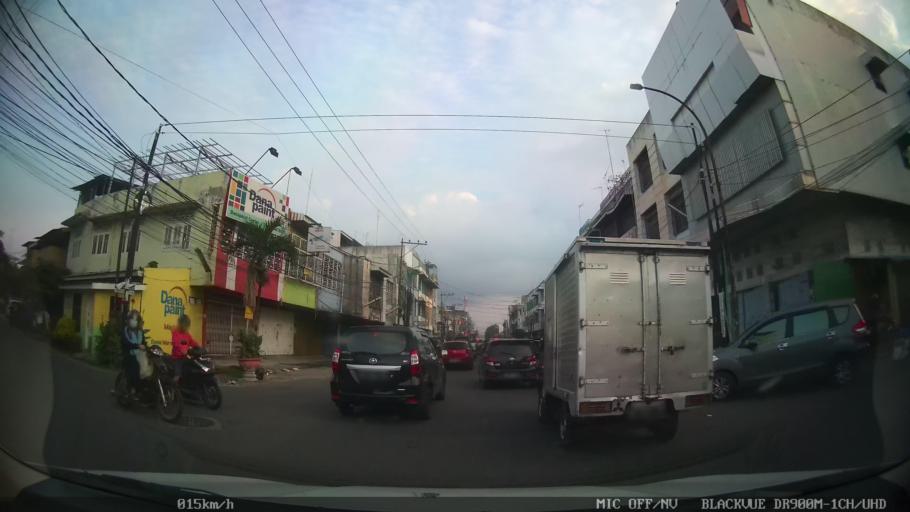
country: ID
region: North Sumatra
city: Medan
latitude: 3.5957
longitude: 98.6879
